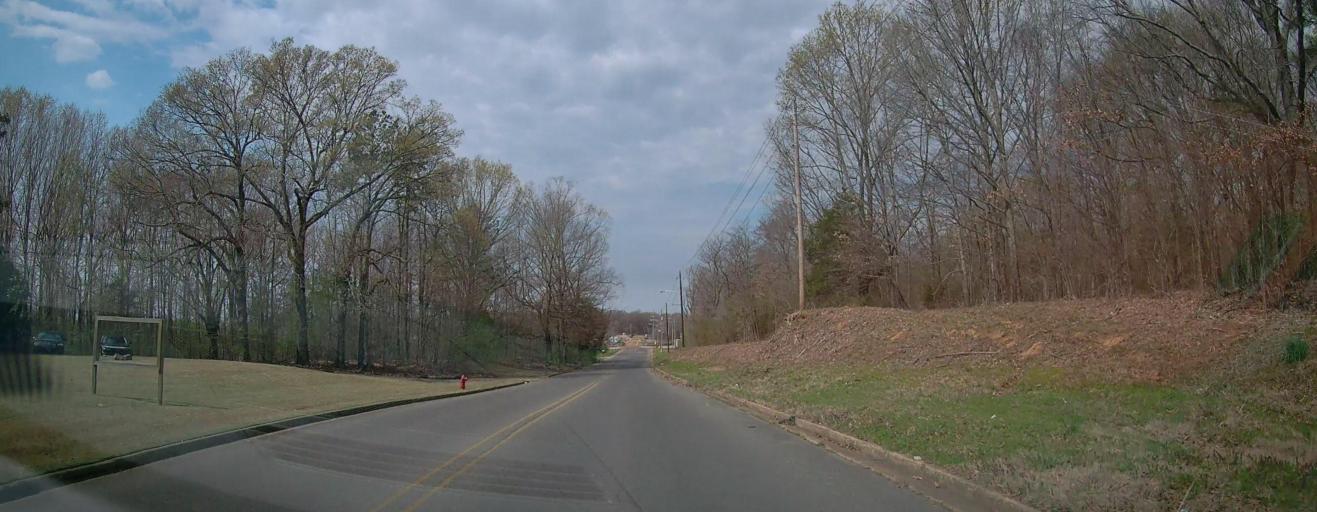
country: US
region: Mississippi
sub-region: De Soto County
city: Olive Branch
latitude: 34.9913
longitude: -89.8590
